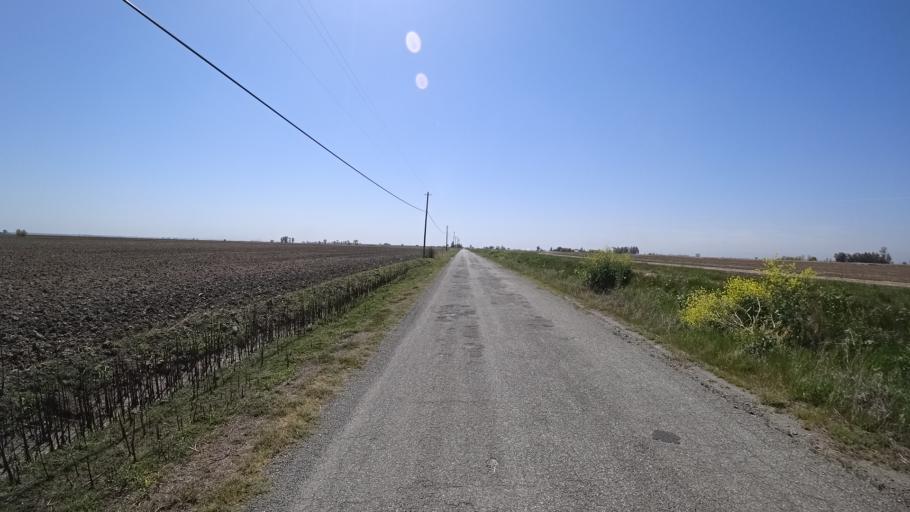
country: US
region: California
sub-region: Glenn County
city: Willows
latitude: 39.5342
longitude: -122.1123
